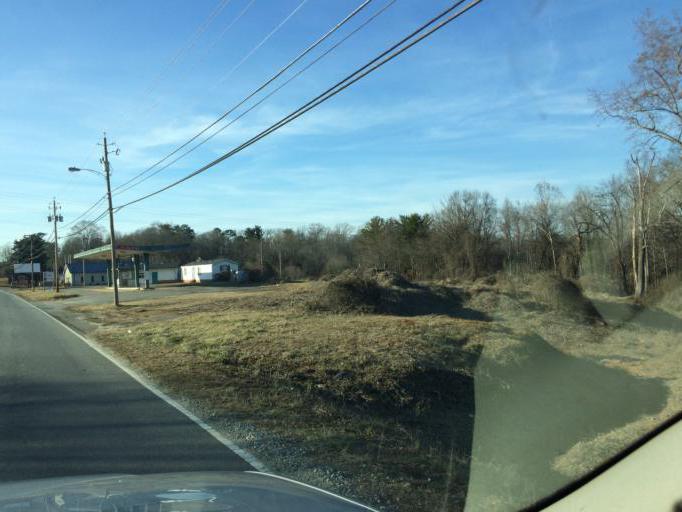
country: US
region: North Carolina
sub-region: Rutherford County
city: Forest City
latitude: 35.3507
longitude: -81.8919
